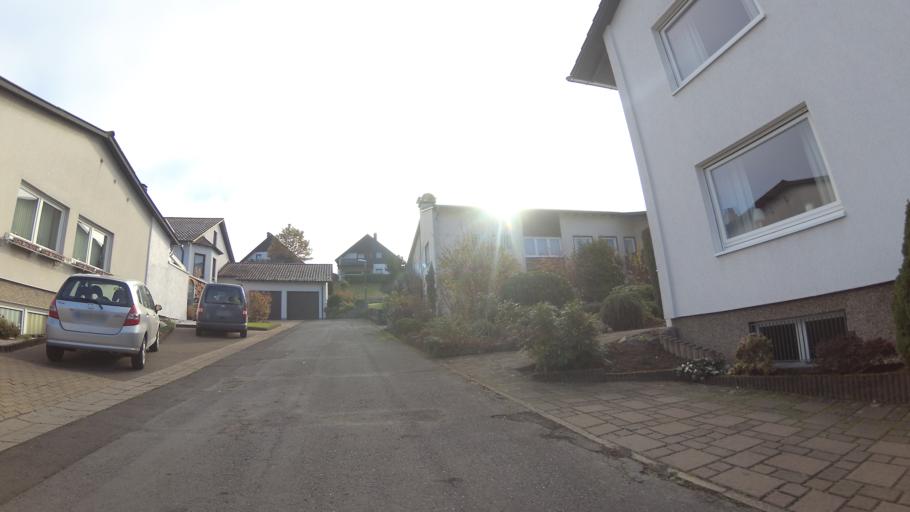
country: DE
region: Saarland
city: Ensdorf
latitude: 49.3084
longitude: 6.7847
